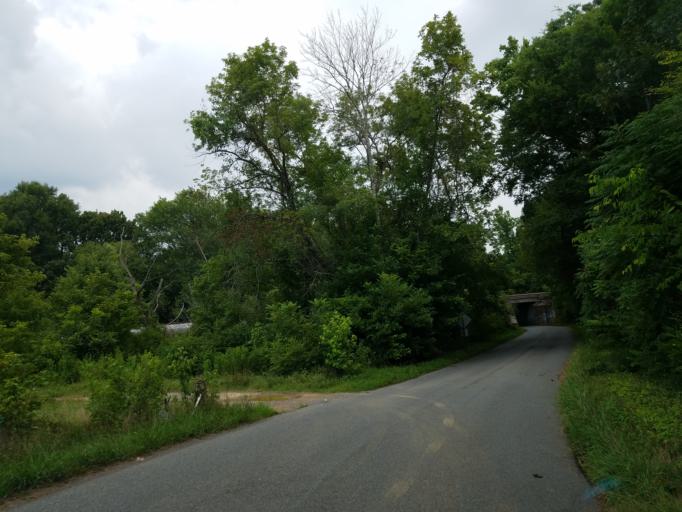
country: US
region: Georgia
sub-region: Bartow County
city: Rydal
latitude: 34.2629
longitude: -84.7609
